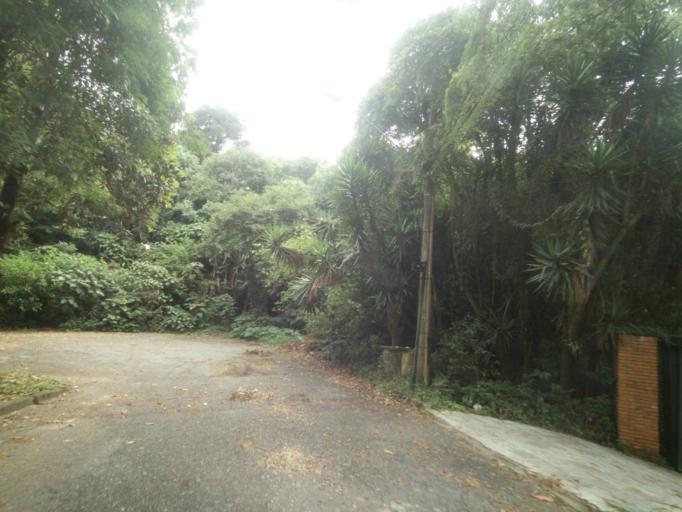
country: BR
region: Parana
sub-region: Curitiba
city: Curitiba
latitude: -25.4142
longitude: -49.3037
